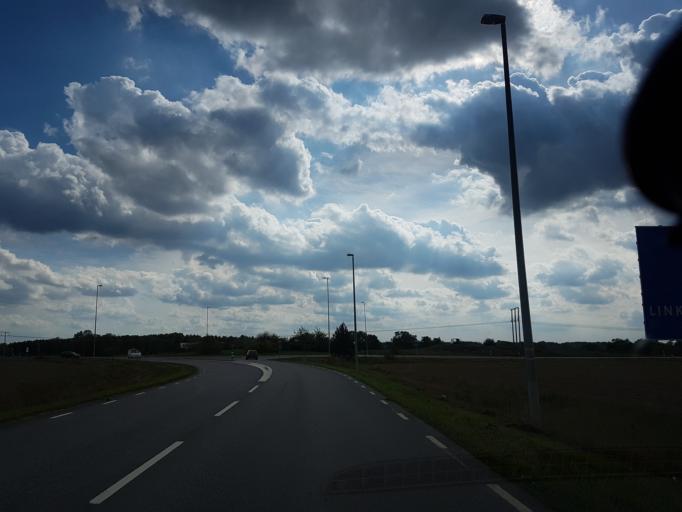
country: SE
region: OEstergoetland
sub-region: Linkopings Kommun
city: Vikingstad
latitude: 58.3776
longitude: 15.4364
